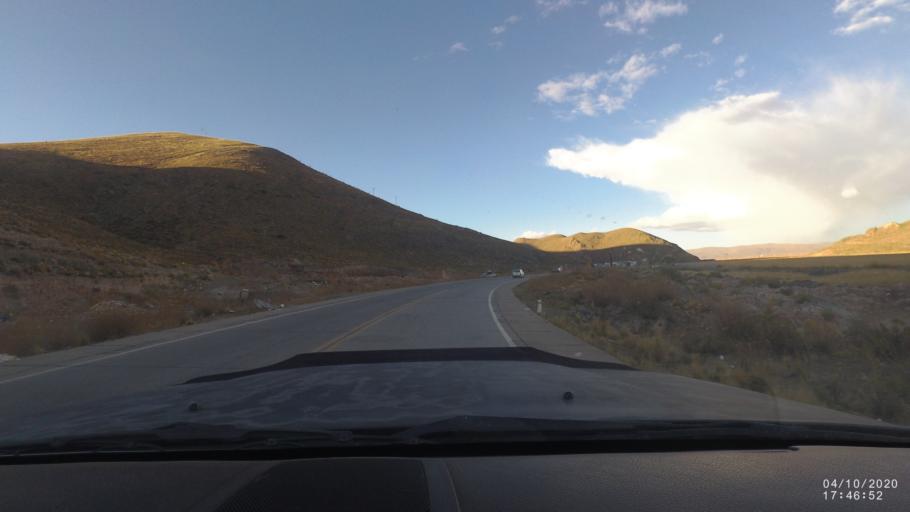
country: BO
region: Oruro
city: Oruro
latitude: -18.0278
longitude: -67.1474
